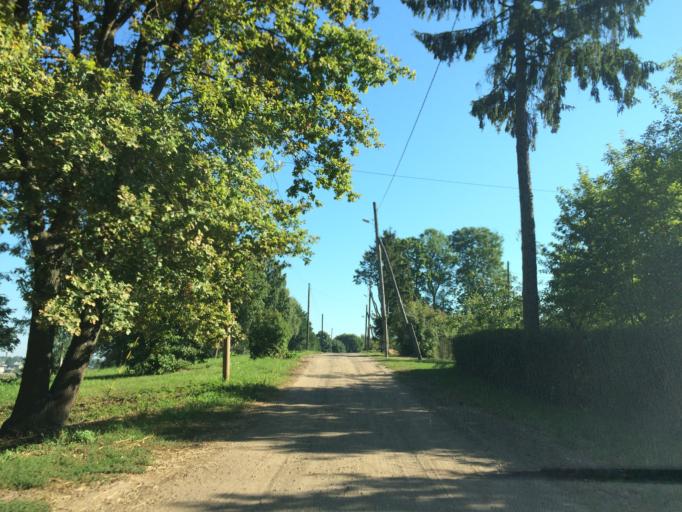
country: LV
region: Rezekne
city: Rezekne
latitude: 56.5075
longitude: 27.3483
